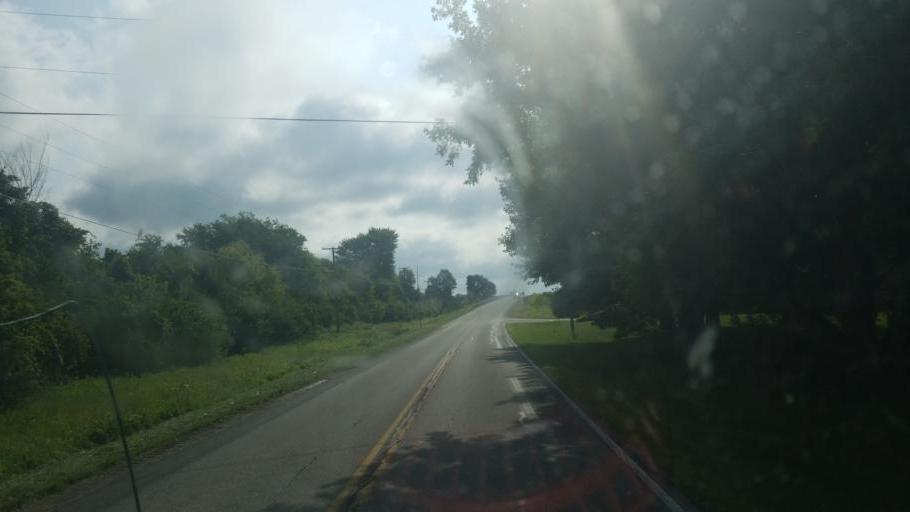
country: US
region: Ohio
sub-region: Marion County
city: Marion
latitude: 40.5692
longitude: -83.0779
